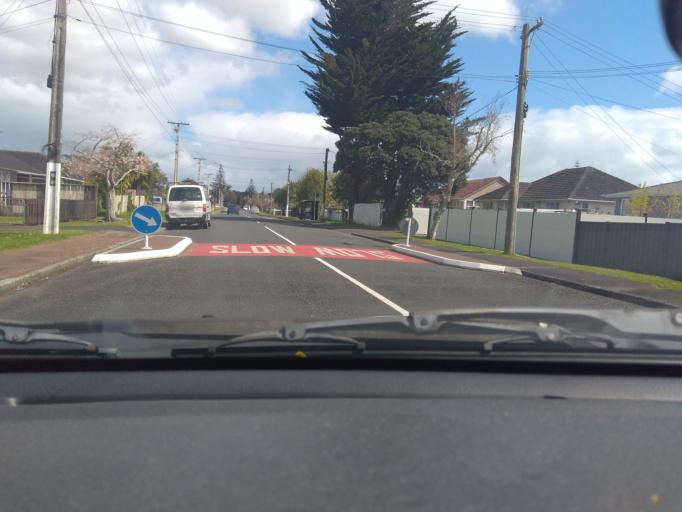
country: NZ
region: Auckland
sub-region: Auckland
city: Tamaki
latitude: -36.9284
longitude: 174.8586
